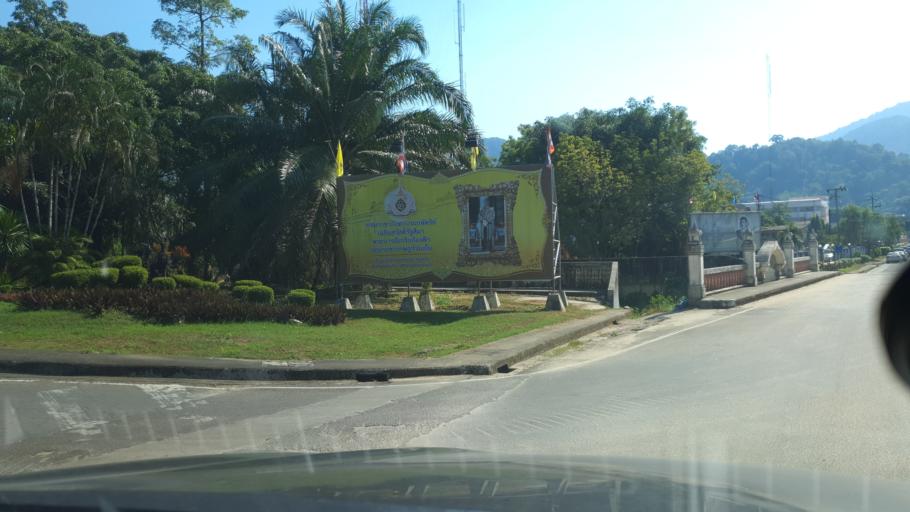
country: TH
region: Ranong
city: Ranong
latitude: 9.9650
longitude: 98.6398
